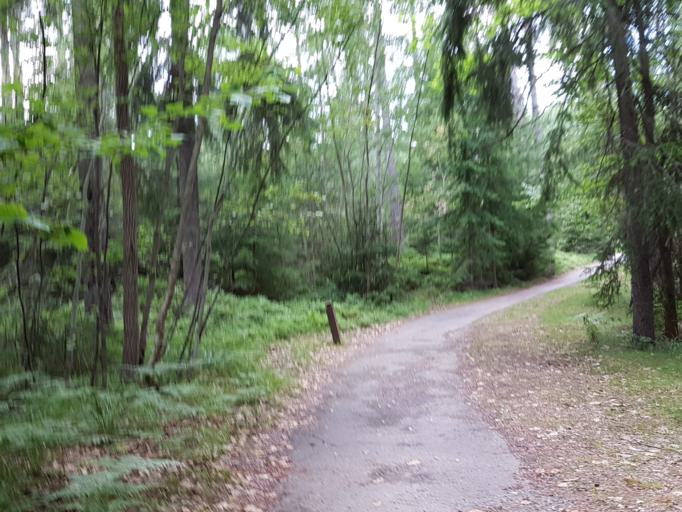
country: SE
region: Stockholm
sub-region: Nacka Kommun
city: Kummelnas
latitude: 59.3472
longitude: 18.2423
